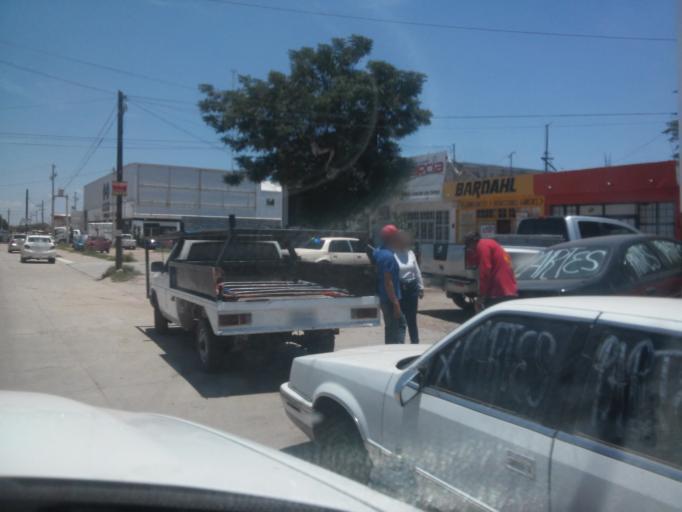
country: MX
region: Durango
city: Victoria de Durango
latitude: 24.0443
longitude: -104.5945
